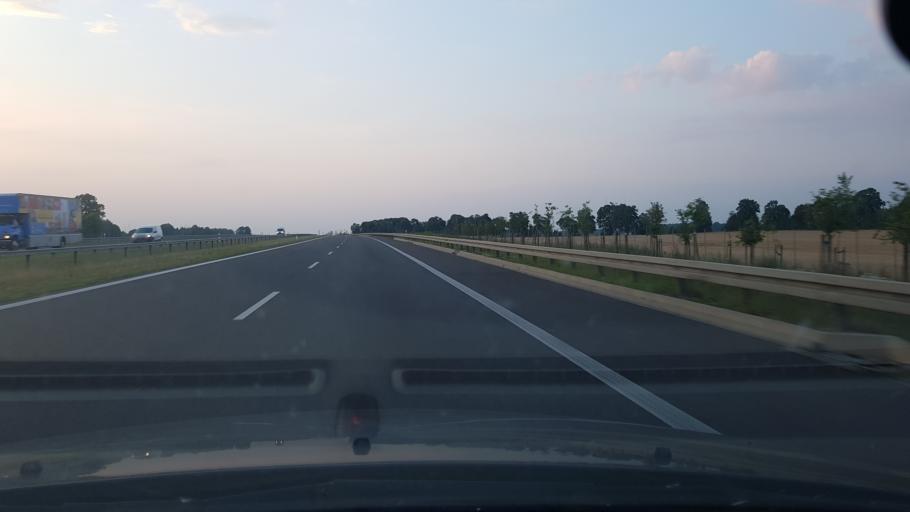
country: PL
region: Warmian-Masurian Voivodeship
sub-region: Powiat nidzicki
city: Nidzica
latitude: 53.2855
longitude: 20.4390
